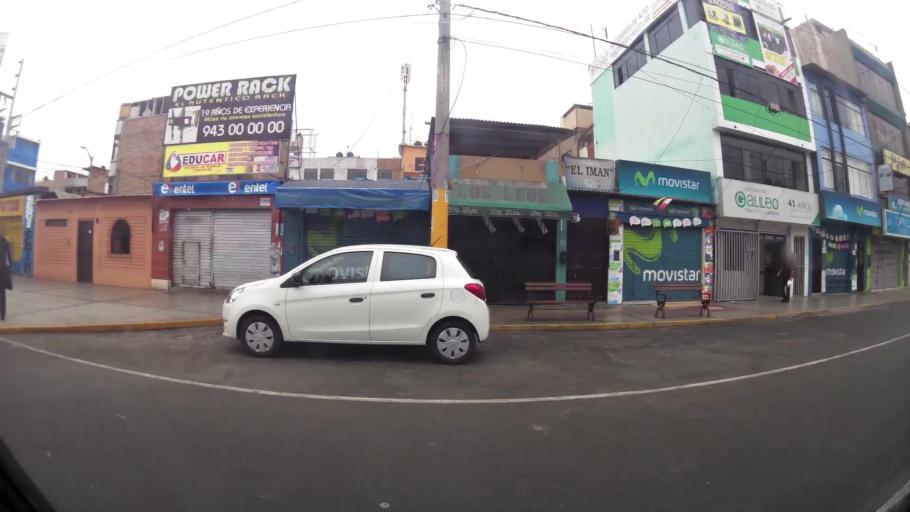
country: PE
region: Ancash
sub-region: Provincia de Santa
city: Chimbote
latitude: -9.0756
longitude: -78.5920
